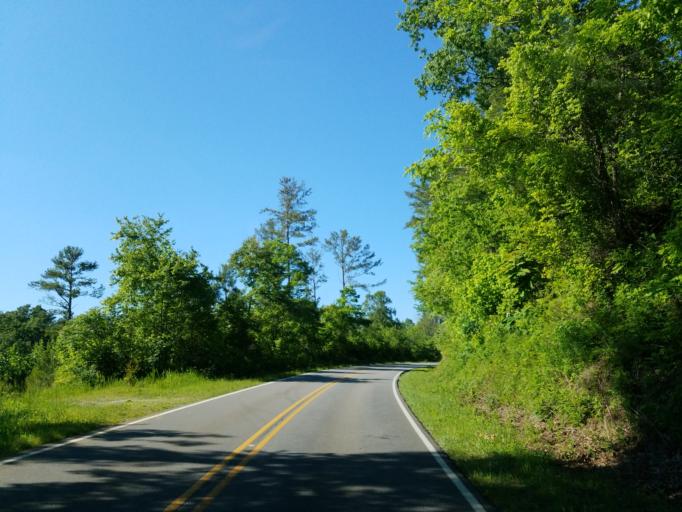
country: US
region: Georgia
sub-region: Pickens County
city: Jasper
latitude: 34.5327
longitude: -84.5088
